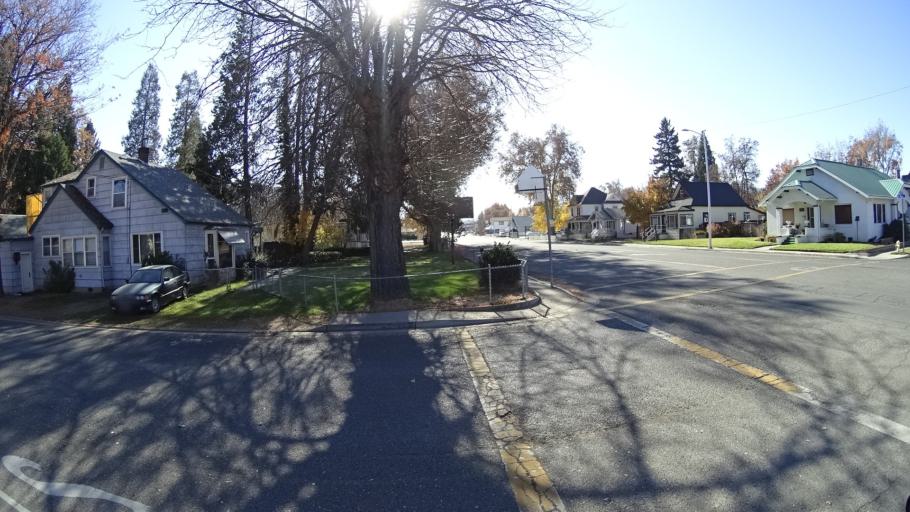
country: US
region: California
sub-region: Siskiyou County
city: Yreka
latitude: 41.7359
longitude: -122.6343
